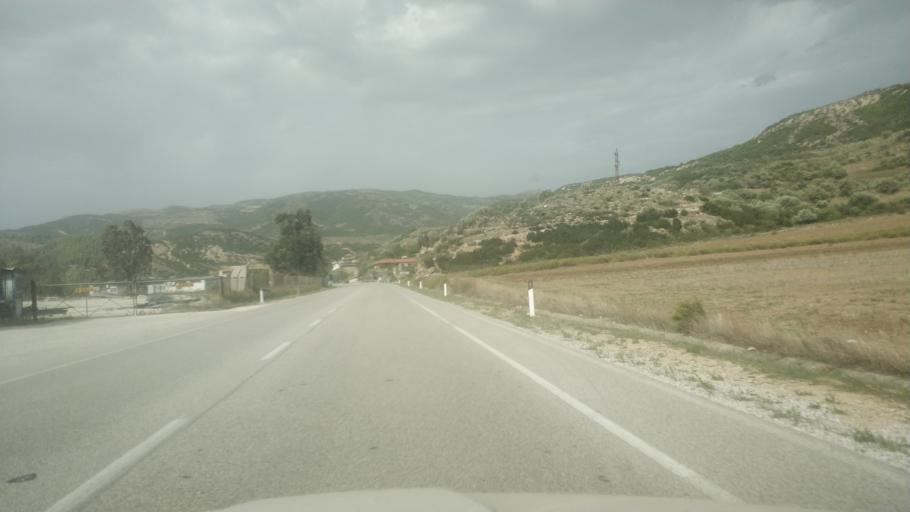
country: AL
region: Gjirokaster
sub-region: Rrethi i Tepelenes
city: Memaliaj
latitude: 40.3718
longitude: 19.9075
